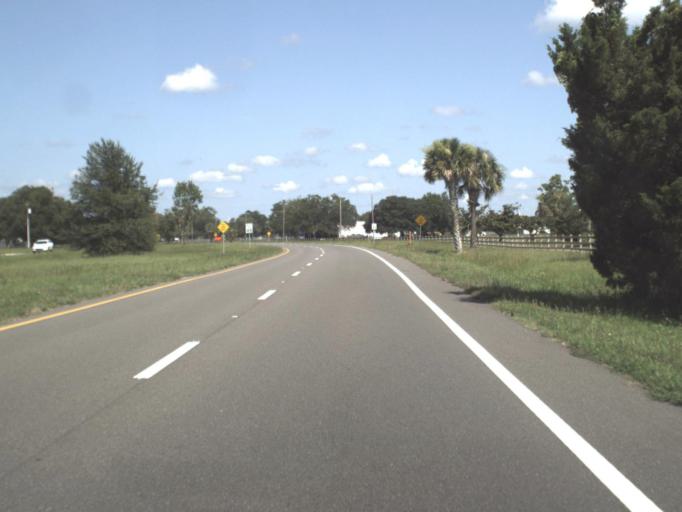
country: US
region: Florida
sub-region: Clay County
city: Green Cove Springs
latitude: 29.9815
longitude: -81.6566
